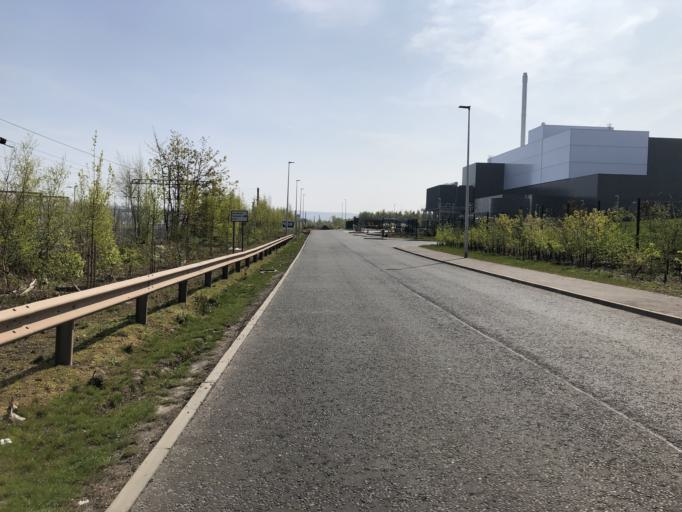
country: GB
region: Scotland
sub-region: Midlothian
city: Dalkeith
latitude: 55.9264
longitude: -3.0852
